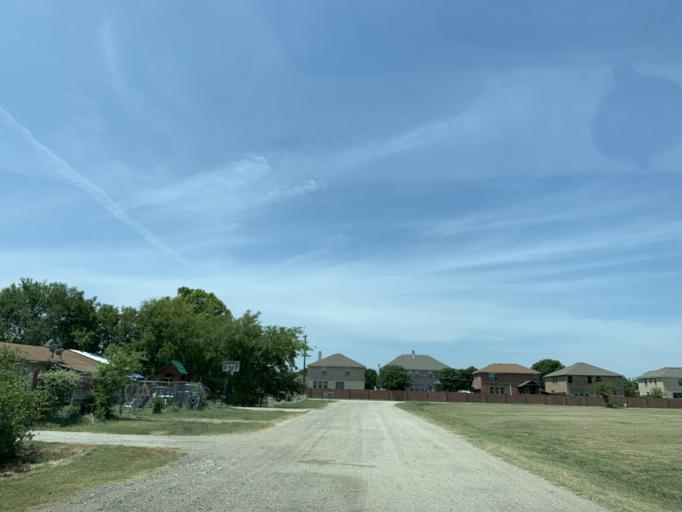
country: US
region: Texas
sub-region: Dallas County
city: Cedar Hill
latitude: 32.6436
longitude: -97.0294
